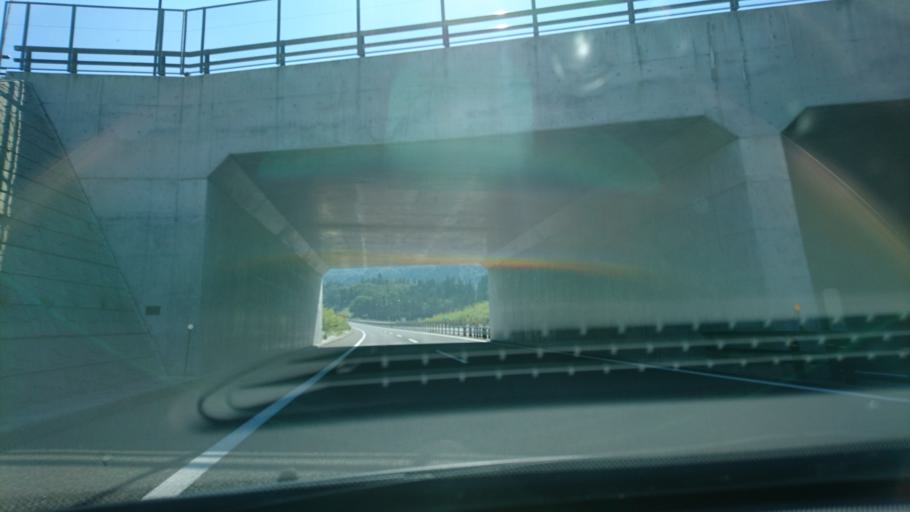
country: JP
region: Iwate
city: Kitakami
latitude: 39.2909
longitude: 141.2732
